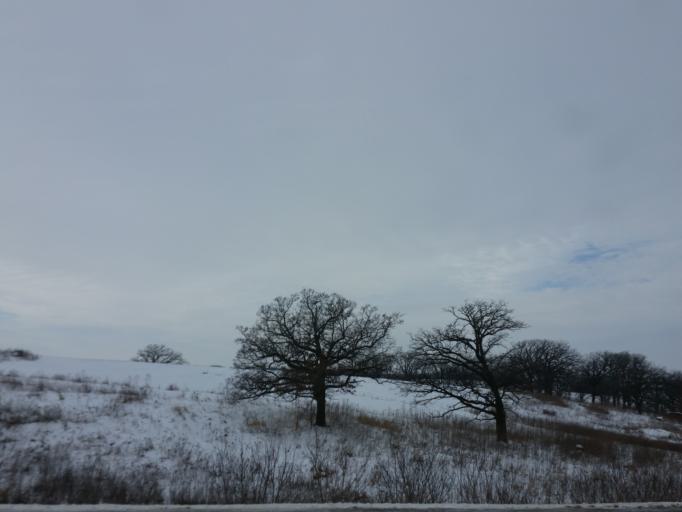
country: US
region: Iowa
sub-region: Dubuque County
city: Peosta
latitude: 42.3992
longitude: -90.8494
